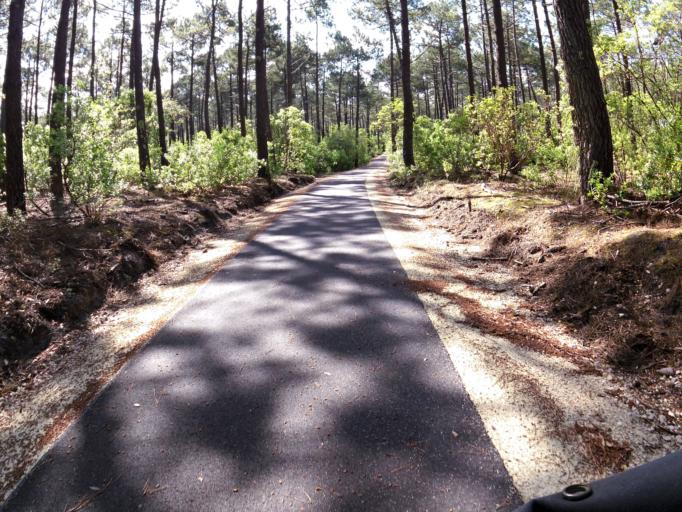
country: FR
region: Aquitaine
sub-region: Departement de la Gironde
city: Lacanau
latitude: 45.0363
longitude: -1.1832
